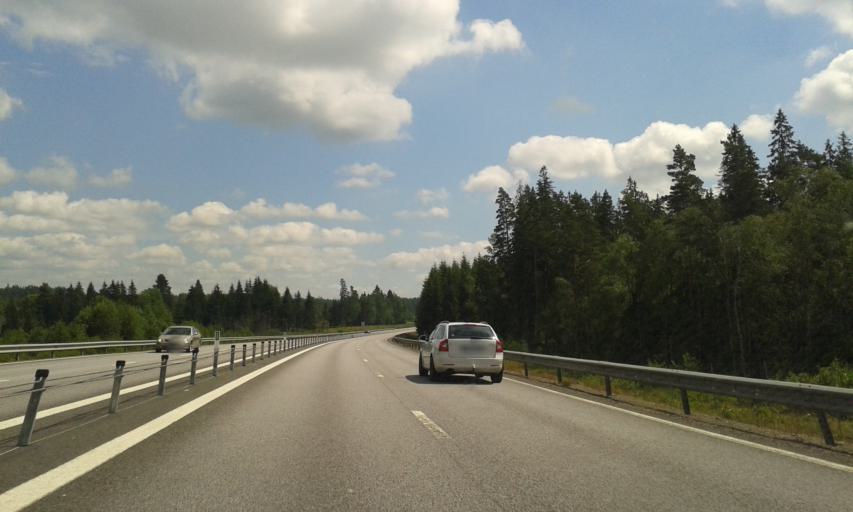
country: SE
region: Kronoberg
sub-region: Alvesta Kommun
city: Alvesta
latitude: 56.9200
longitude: 14.6057
